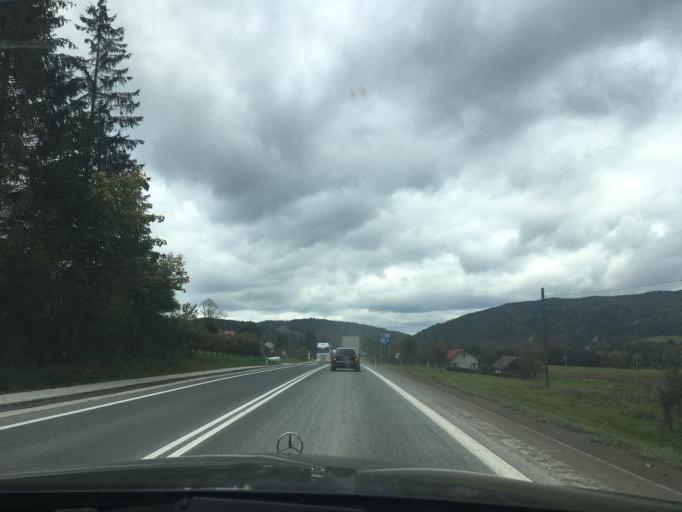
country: PL
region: Subcarpathian Voivodeship
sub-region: Powiat krosnienski
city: Dukla
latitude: 49.4978
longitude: 21.7009
